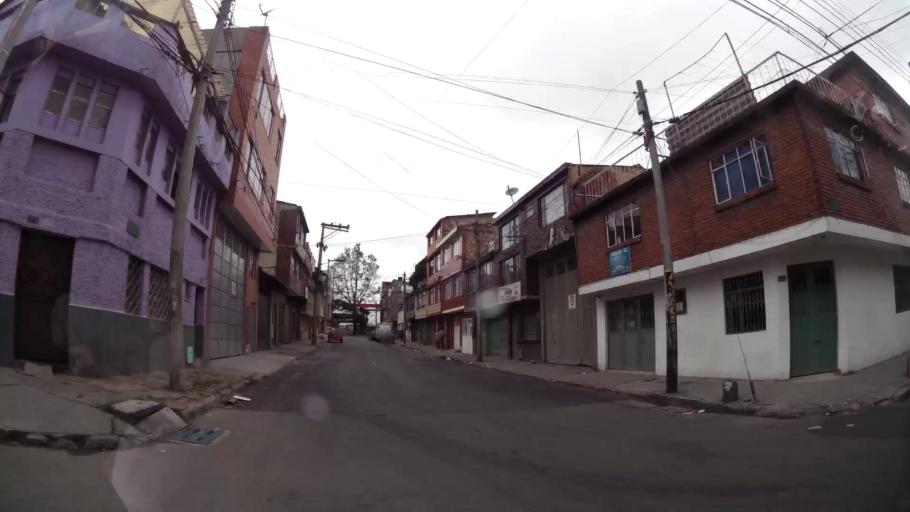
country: CO
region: Bogota D.C.
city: Barrio San Luis
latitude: 4.6783
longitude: -74.0878
